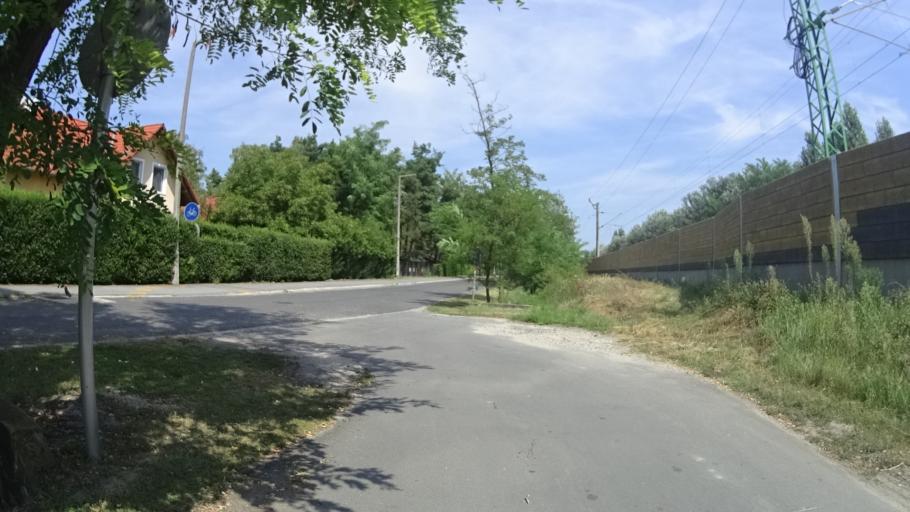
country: HU
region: Somogy
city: Fonyod
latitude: 46.7625
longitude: 17.6028
